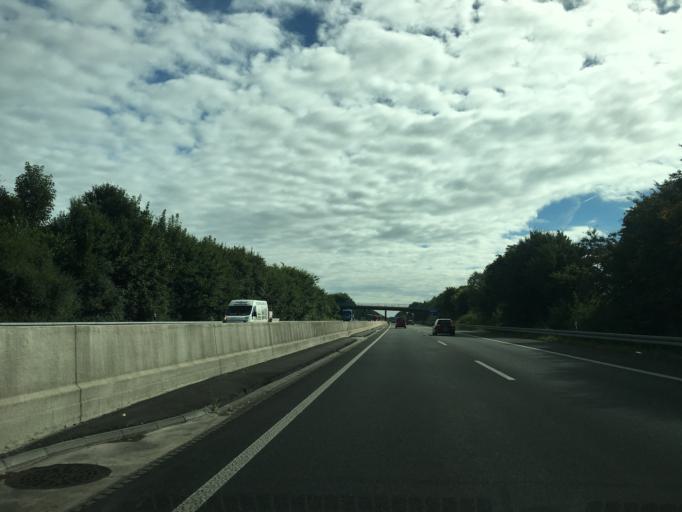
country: DE
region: North Rhine-Westphalia
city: Spenge
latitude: 52.1924
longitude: 8.5147
